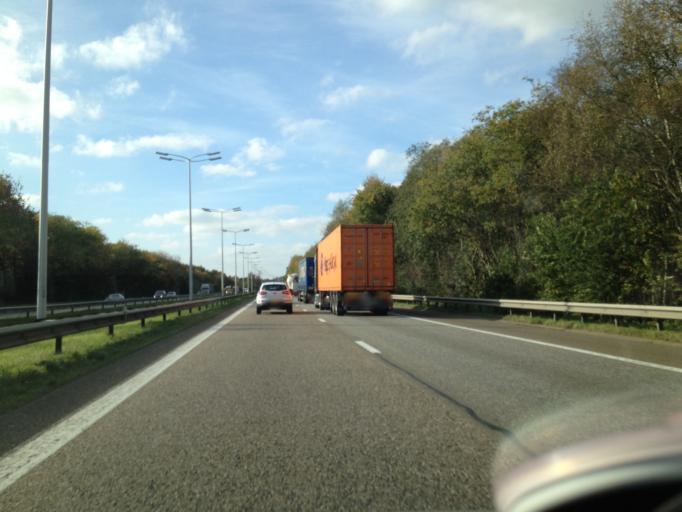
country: BE
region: Flanders
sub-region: Provincie Limburg
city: Maasmechelen
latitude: 50.9549
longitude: 5.6761
